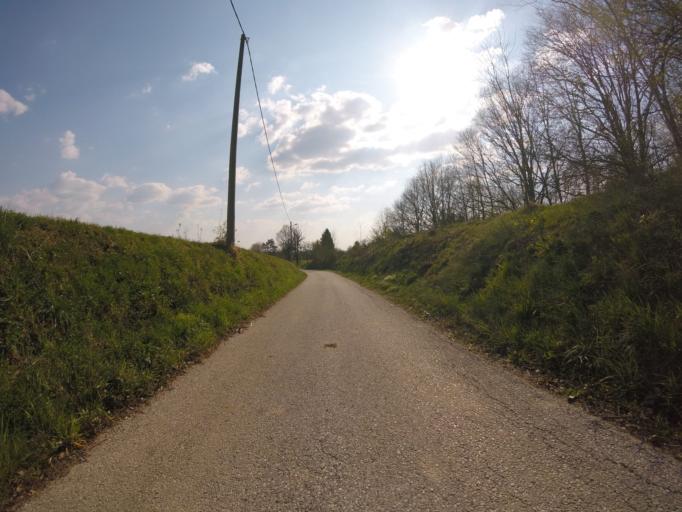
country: HR
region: Sisacko-Moslavacka
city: Glina
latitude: 45.4961
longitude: 16.0038
